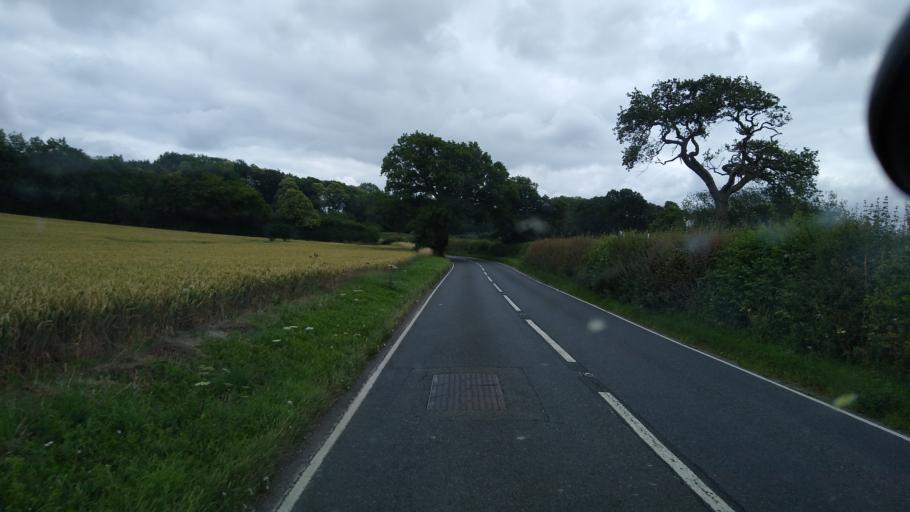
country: GB
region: England
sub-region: Hampshire
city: Alton
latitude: 51.1313
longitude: -0.9632
